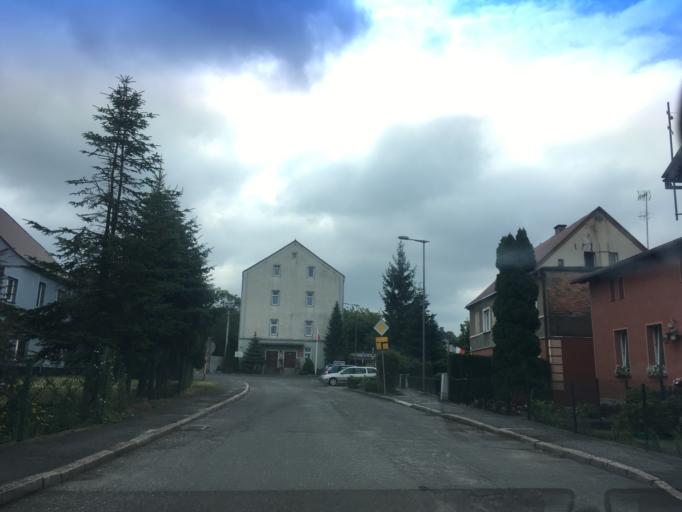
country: PL
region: Lower Silesian Voivodeship
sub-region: Powiat zgorzelecki
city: Sulikow
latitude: 51.0784
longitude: 15.0672
